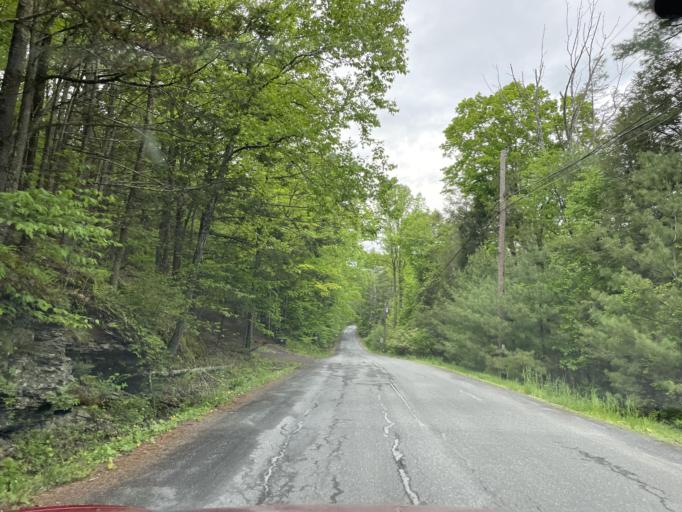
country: US
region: New York
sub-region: Ulster County
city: Woodstock
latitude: 42.0312
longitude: -74.1419
